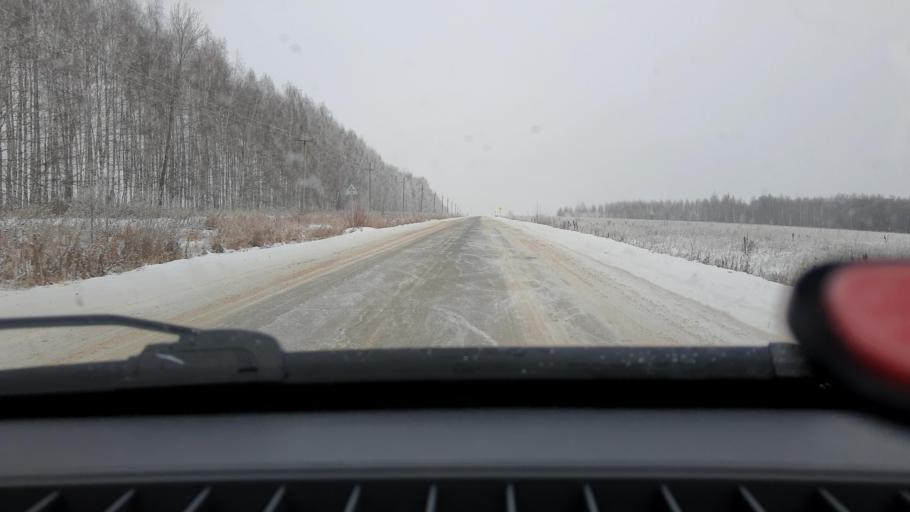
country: RU
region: Bashkortostan
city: Iglino
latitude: 54.6521
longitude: 56.4267
